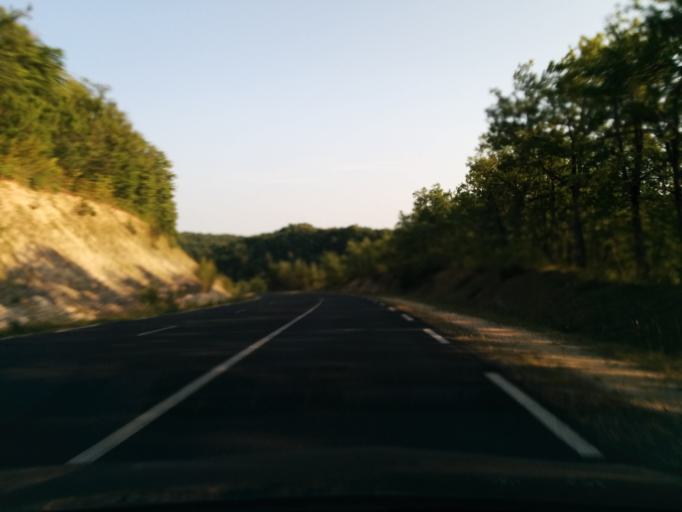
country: FR
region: Midi-Pyrenees
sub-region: Departement du Lot
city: Le Vigan
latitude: 44.7162
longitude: 1.4818
